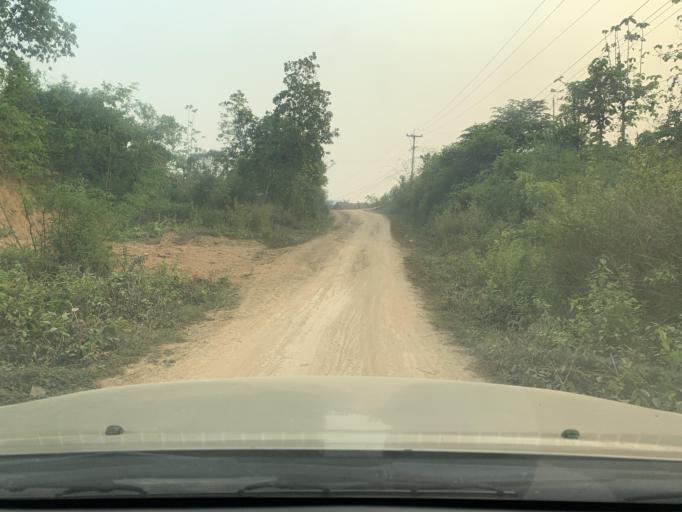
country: LA
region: Louangphabang
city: Louangphabang
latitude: 19.9195
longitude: 102.0756
